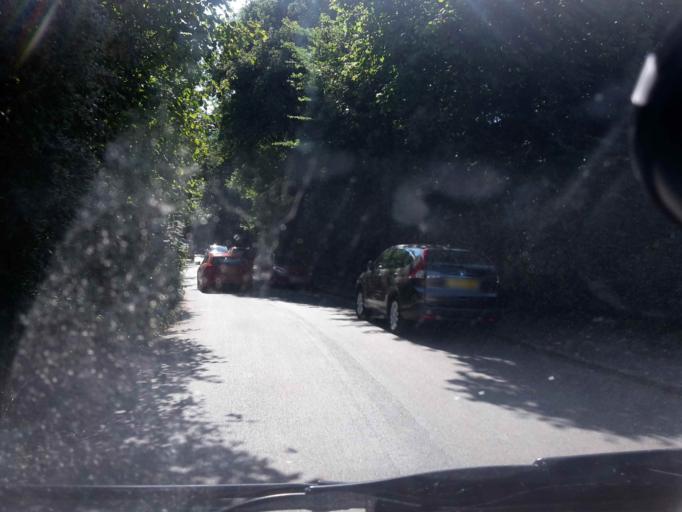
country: GB
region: England
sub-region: Surrey
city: East Horsley
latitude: 51.2180
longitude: -0.4657
